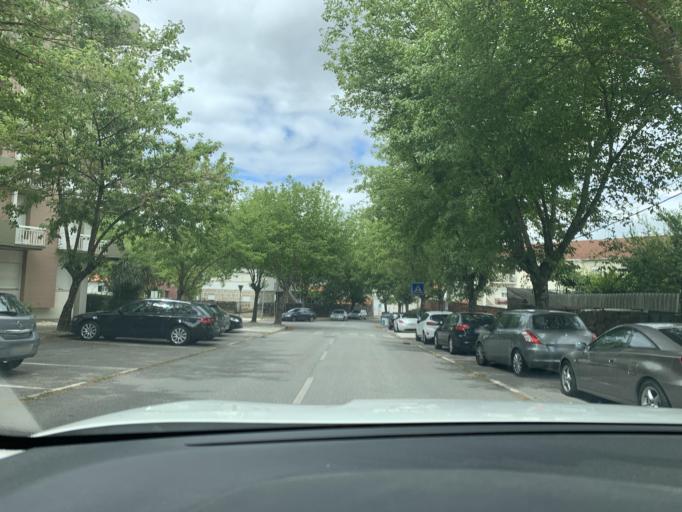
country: PT
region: Viseu
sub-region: Viseu
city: Viseu
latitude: 40.6585
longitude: -7.9283
